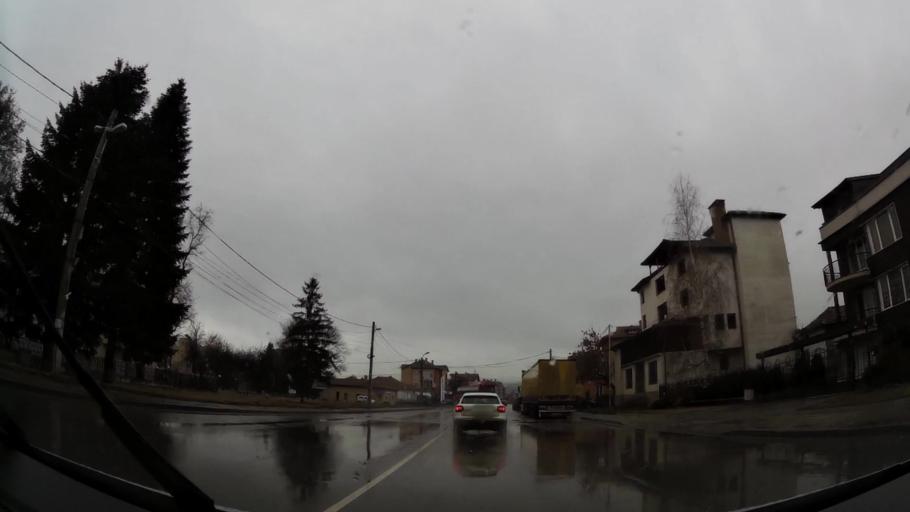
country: BG
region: Sofia-Capital
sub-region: Stolichna Obshtina
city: Sofia
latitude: 42.6260
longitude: 23.4067
